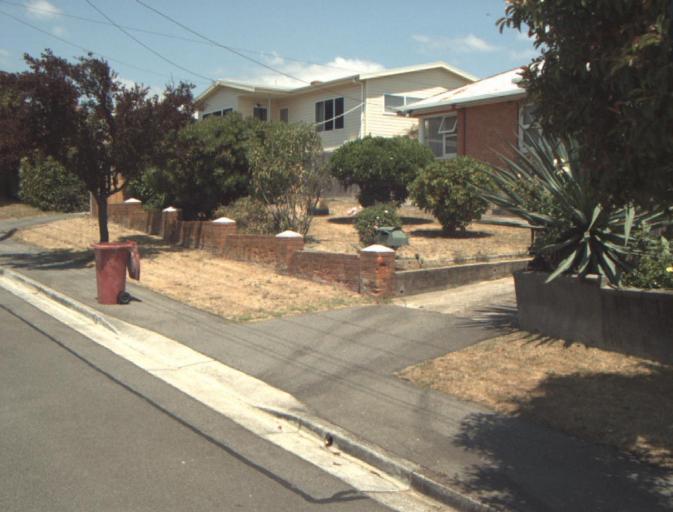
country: AU
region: Tasmania
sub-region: Launceston
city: Summerhill
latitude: -41.4863
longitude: 147.1709
